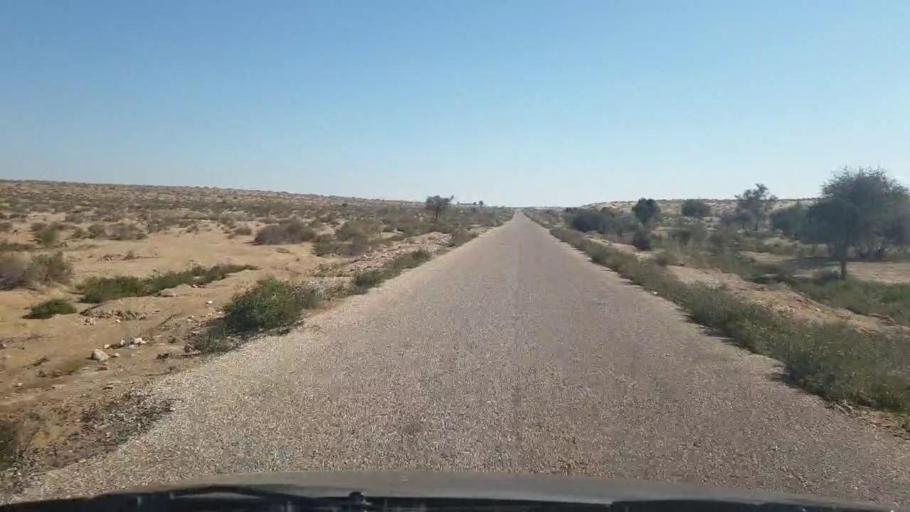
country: PK
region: Sindh
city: Bozdar
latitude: 27.0186
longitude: 68.7753
